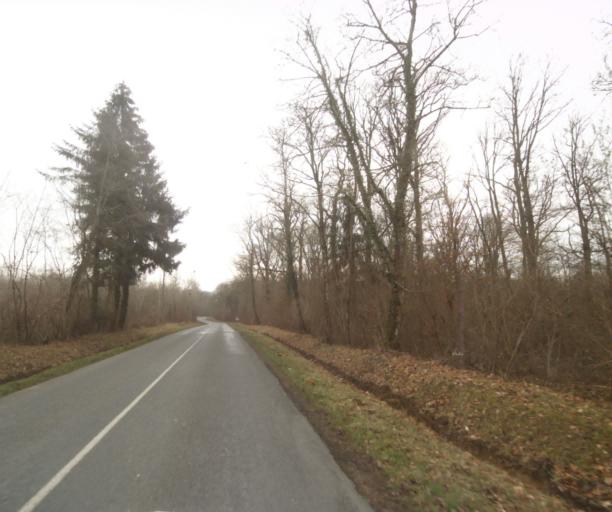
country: FR
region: Champagne-Ardenne
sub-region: Departement de la Marne
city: Pargny-sur-Saulx
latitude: 48.7341
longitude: 4.8623
